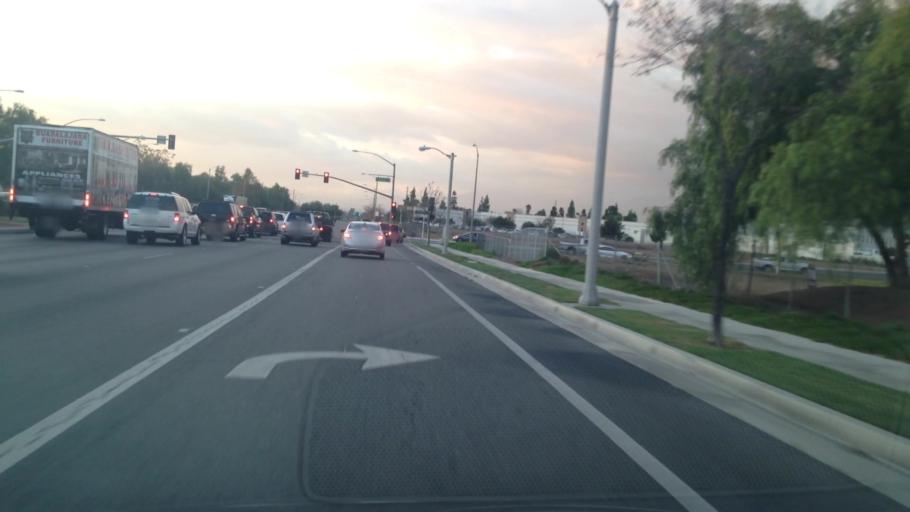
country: US
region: California
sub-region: Riverside County
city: Pedley
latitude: 33.9549
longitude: -117.4560
